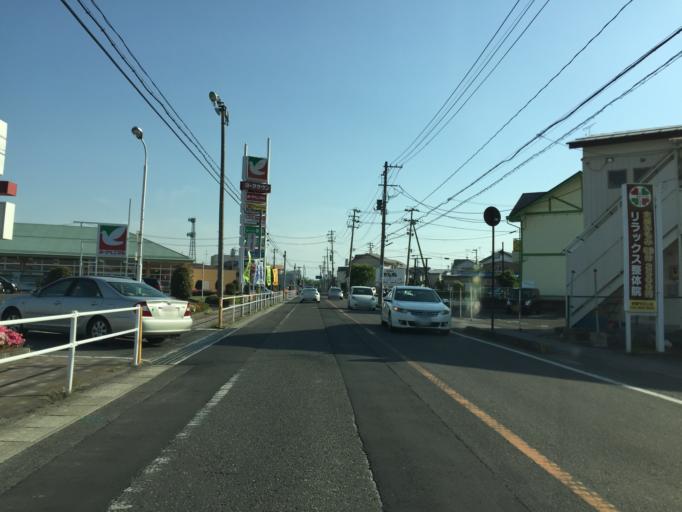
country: JP
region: Fukushima
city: Koriyama
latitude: 37.4026
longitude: 140.3271
